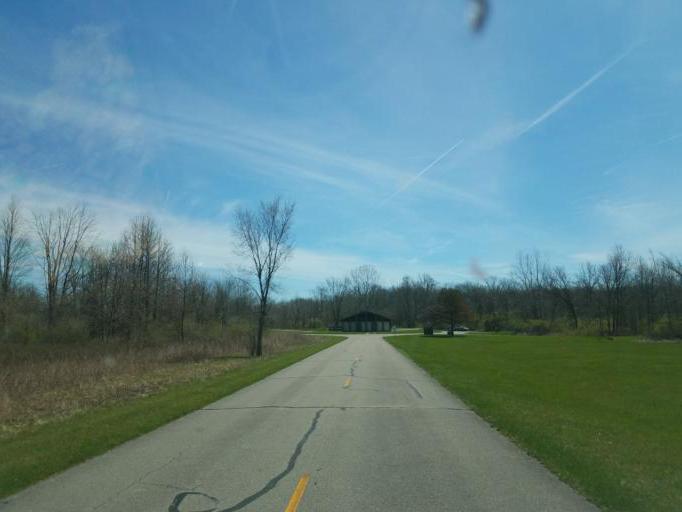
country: US
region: Ohio
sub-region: Delaware County
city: Delaware
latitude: 40.4030
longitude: -83.0612
